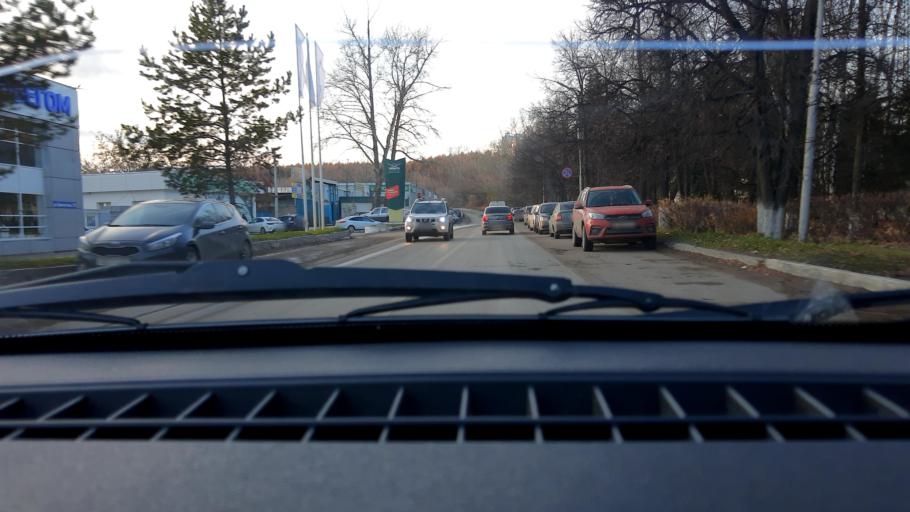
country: RU
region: Bashkortostan
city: Ufa
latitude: 54.8079
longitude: 56.0660
